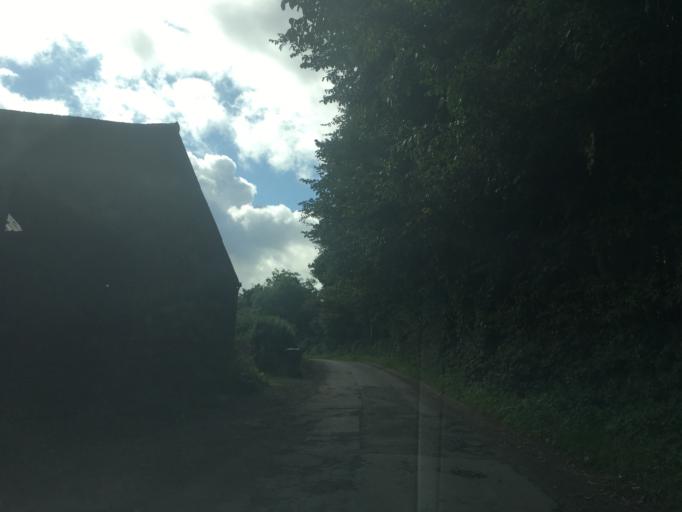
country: GB
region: Scotland
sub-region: Edinburgh
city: Queensferry
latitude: 55.9741
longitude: -3.3525
